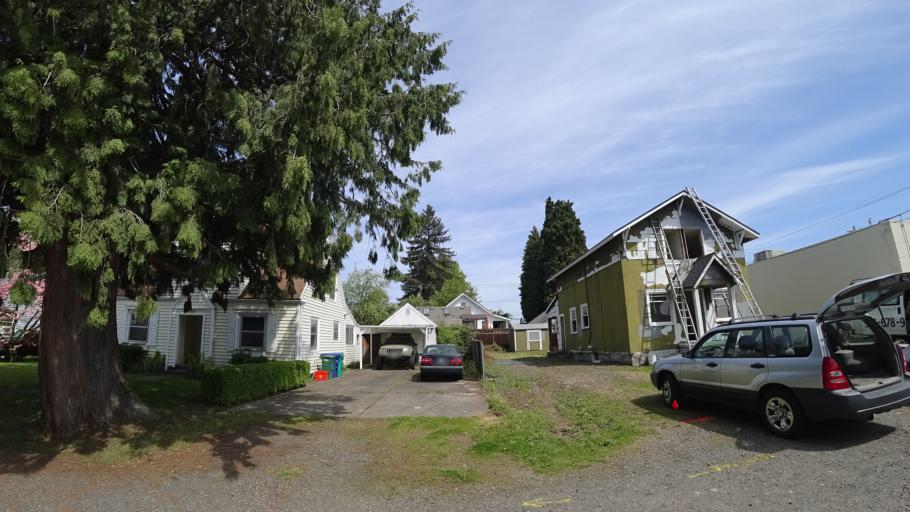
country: US
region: Oregon
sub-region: Clackamas County
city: Milwaukie
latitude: 45.4473
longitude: -122.6203
